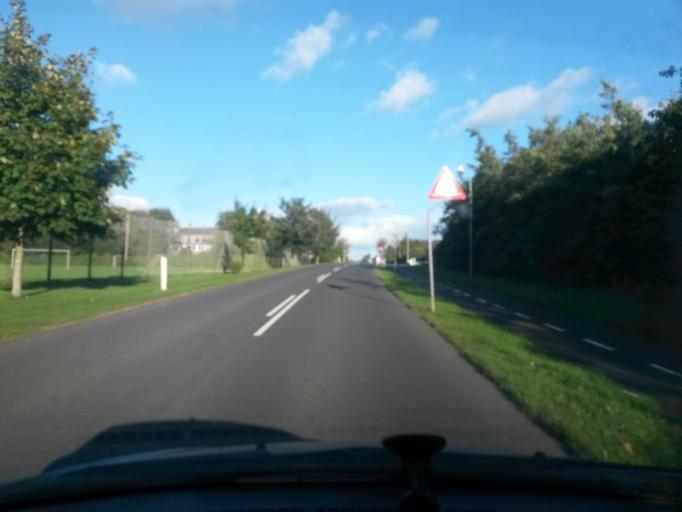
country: DK
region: Central Jutland
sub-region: Silkeborg Kommune
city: Kjellerup
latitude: 56.3284
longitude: 9.3514
